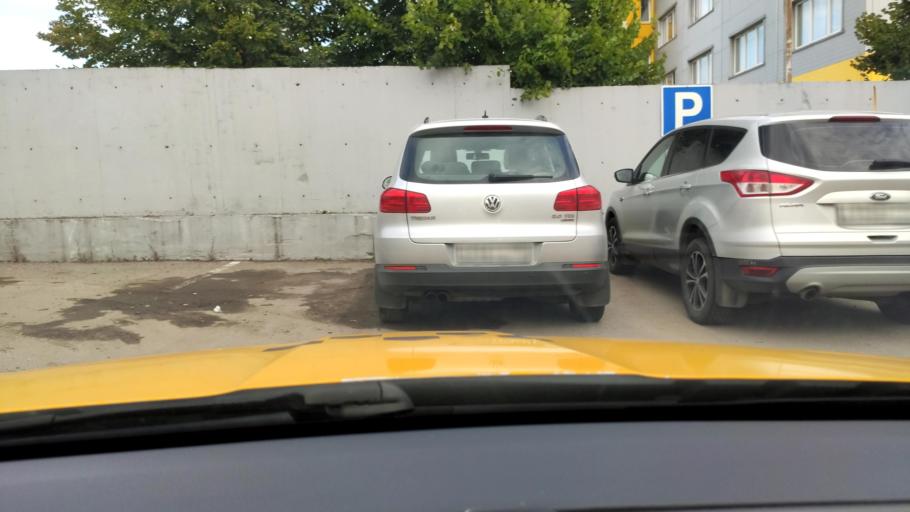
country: RU
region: Moskovskaya
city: Kozhukhovo
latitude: 55.7065
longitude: 37.7037
